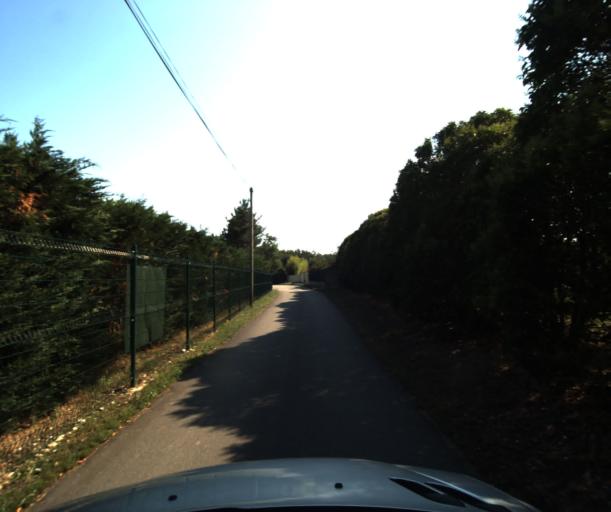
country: FR
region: Midi-Pyrenees
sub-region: Departement de la Haute-Garonne
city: Lacroix-Falgarde
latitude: 43.4795
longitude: 1.4043
